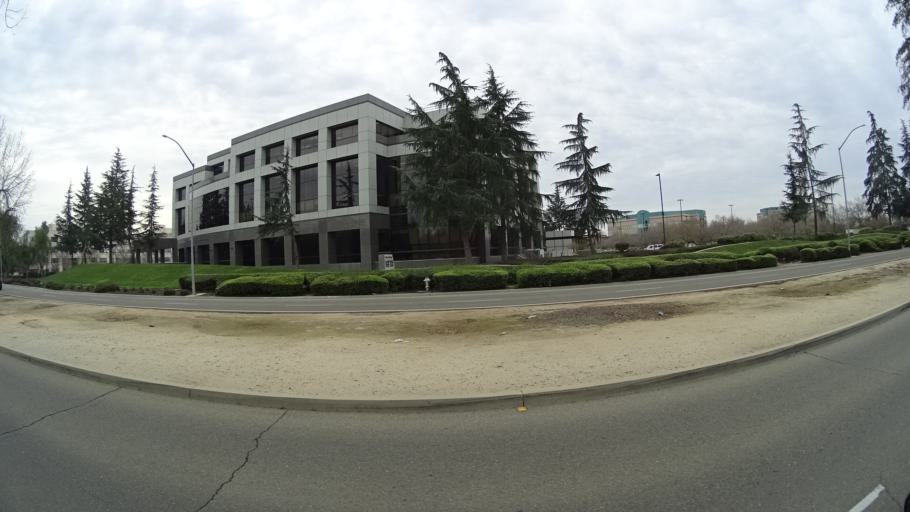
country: US
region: California
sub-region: Fresno County
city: Clovis
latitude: 36.8614
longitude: -119.7857
